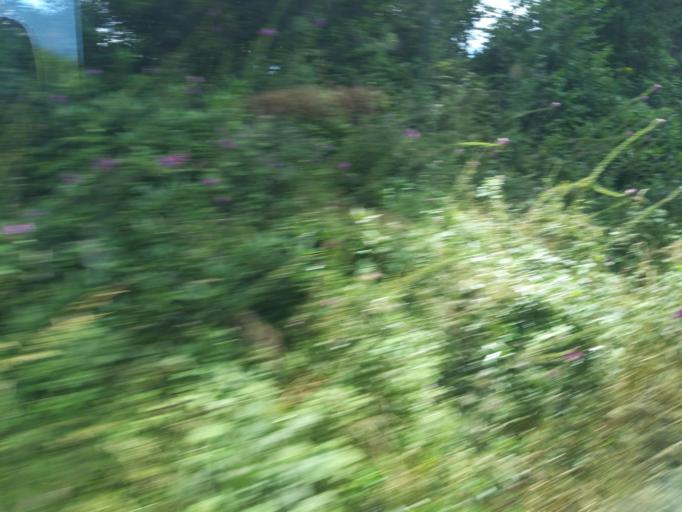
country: GB
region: England
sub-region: Cornwall
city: Par
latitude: 50.3662
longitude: -4.6865
